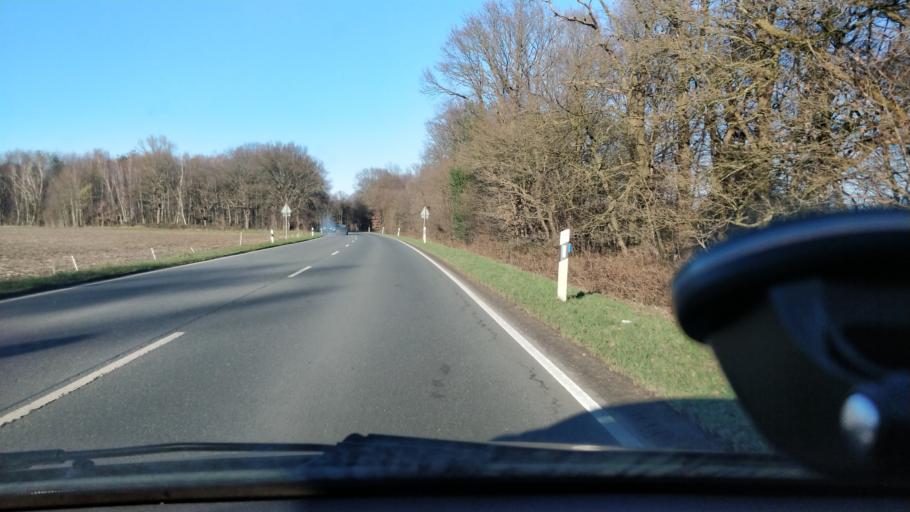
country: DE
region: North Rhine-Westphalia
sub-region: Regierungsbezirk Munster
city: Bottrop
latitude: 51.5755
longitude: 6.8807
